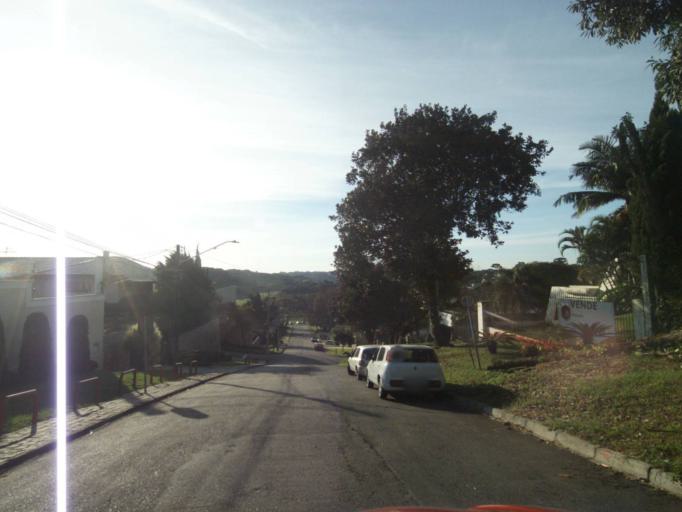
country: BR
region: Parana
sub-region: Curitiba
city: Curitiba
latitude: -25.4307
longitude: -49.3051
